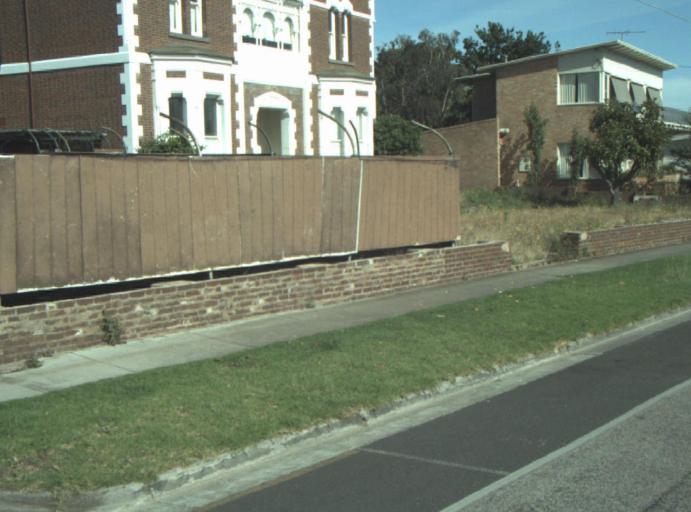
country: AU
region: Victoria
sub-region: Greater Geelong
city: Geelong West
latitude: -38.1377
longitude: 144.3554
